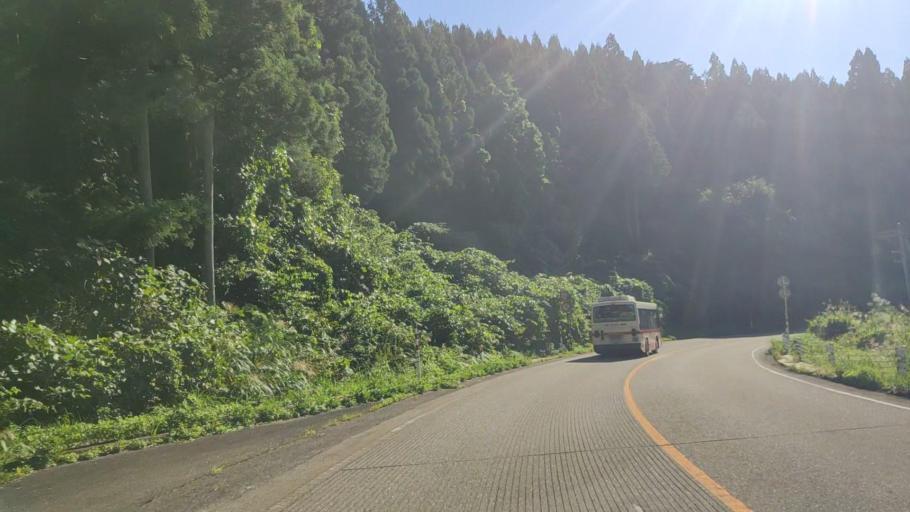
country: JP
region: Ishikawa
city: Nanao
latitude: 37.2420
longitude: 136.9879
